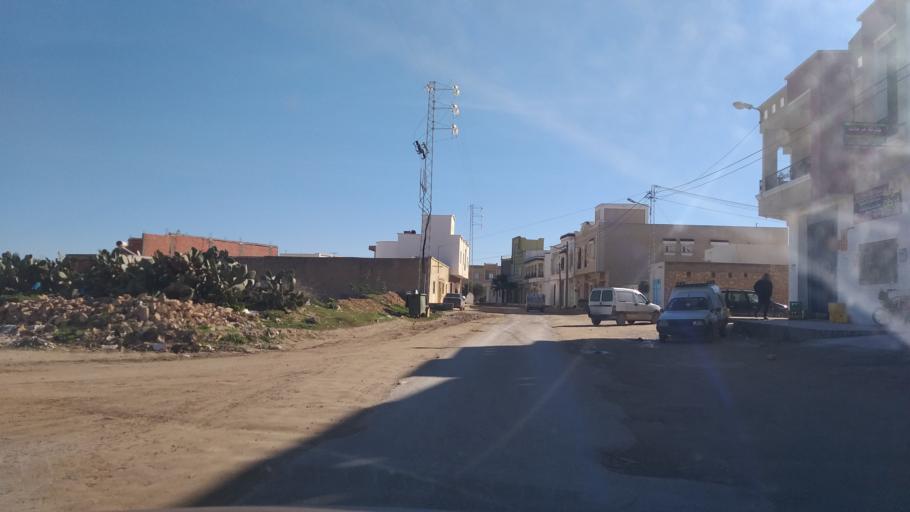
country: TN
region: Al Mahdiyah
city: El Jem
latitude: 35.2935
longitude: 10.7155
